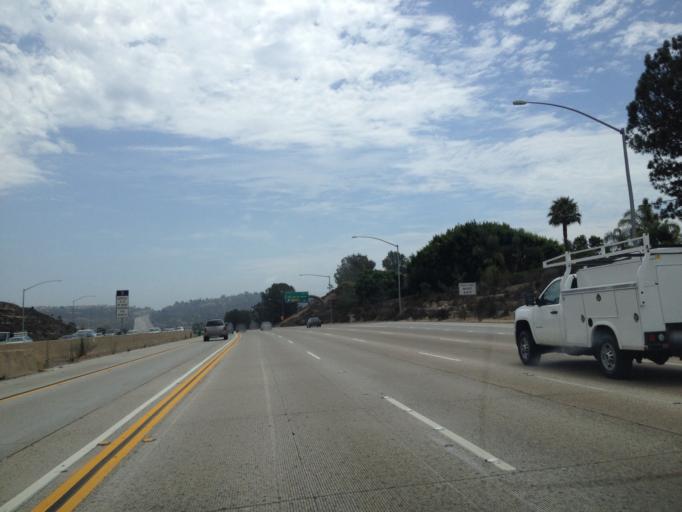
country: US
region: California
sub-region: San Diego County
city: Solana Beach
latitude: 32.9859
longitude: -117.2549
